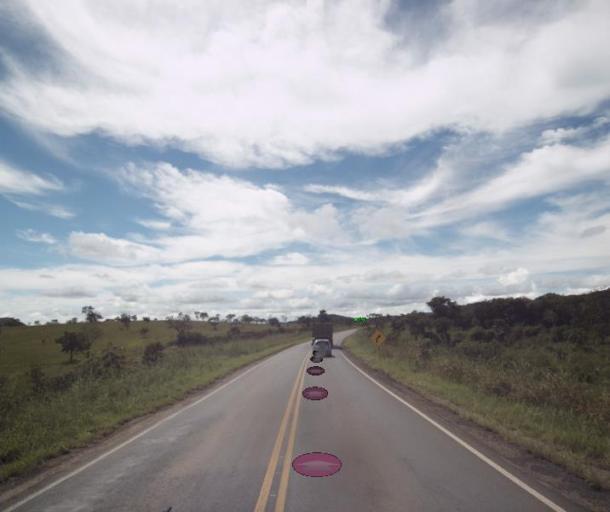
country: BR
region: Goias
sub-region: Padre Bernardo
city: Padre Bernardo
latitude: -15.4656
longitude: -48.2260
